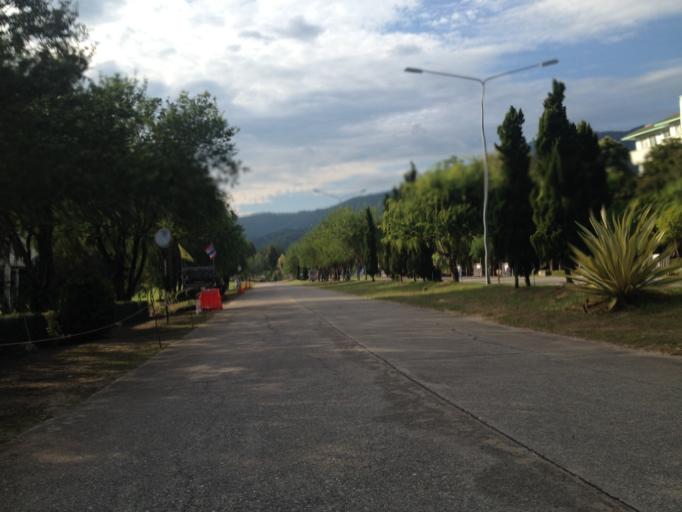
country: TH
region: Chiang Mai
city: Chiang Mai
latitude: 18.7607
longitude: 98.9364
